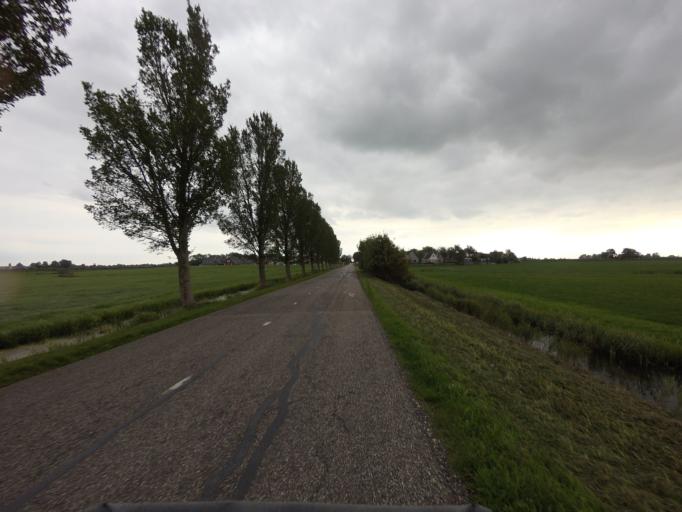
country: NL
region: Friesland
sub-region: Sudwest Fryslan
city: IJlst
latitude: 53.0206
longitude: 5.5986
